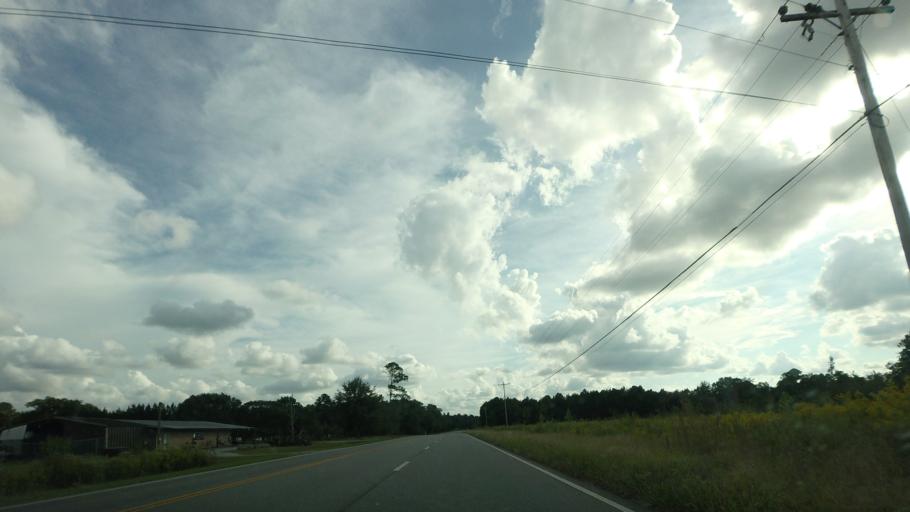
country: US
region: Georgia
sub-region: Pulaski County
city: Hawkinsville
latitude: 32.3134
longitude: -83.4200
